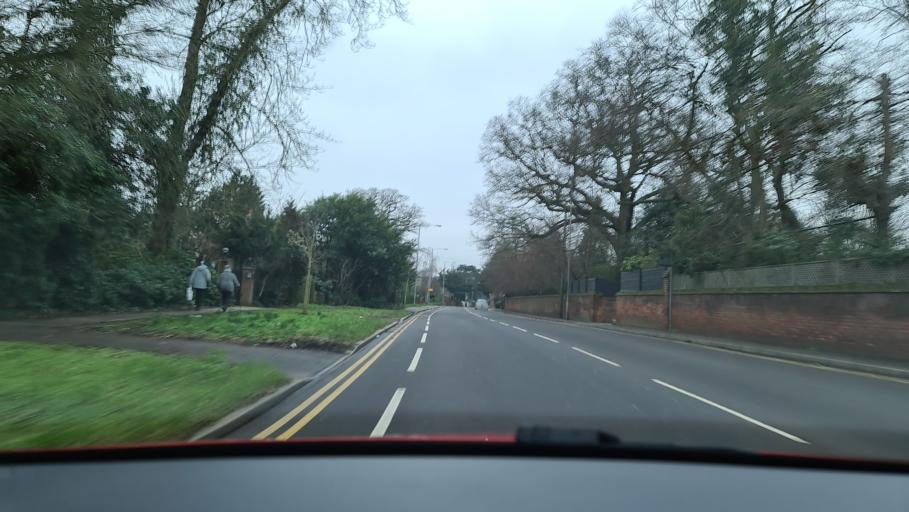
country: GB
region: England
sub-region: Greater London
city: New Malden
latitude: 51.4164
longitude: -0.2552
